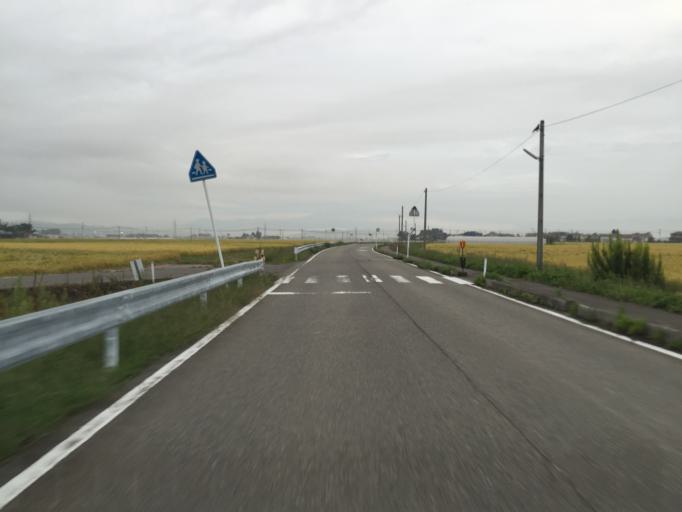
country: JP
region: Fukushima
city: Kitakata
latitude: 37.5499
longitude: 139.8737
